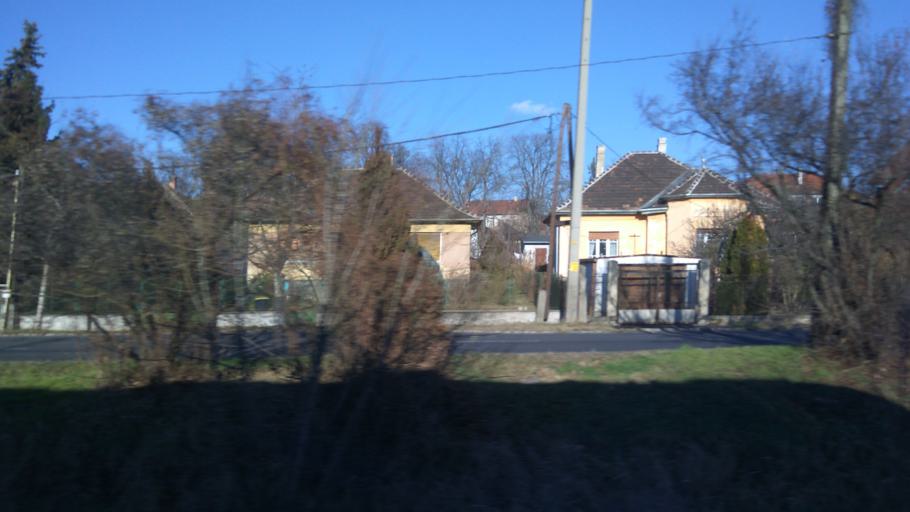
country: HU
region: Budapest
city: Budapest XVII. keruelet
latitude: 47.4871
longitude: 19.2509
